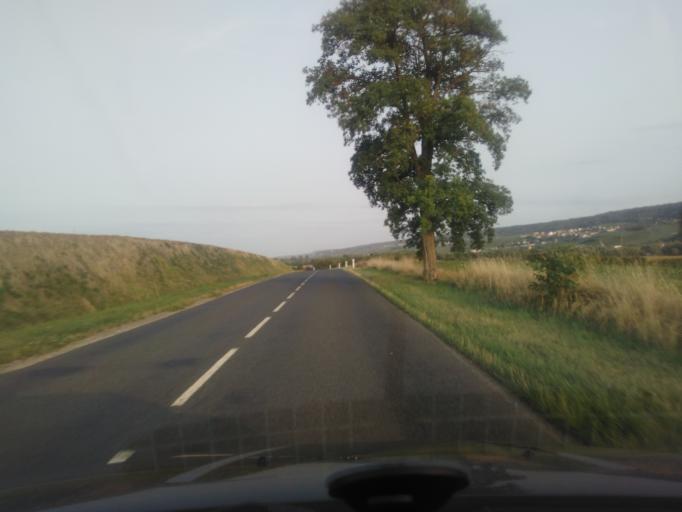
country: FR
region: Champagne-Ardenne
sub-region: Departement de la Marne
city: Mareuil-le-Port
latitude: 49.0891
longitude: 3.7712
